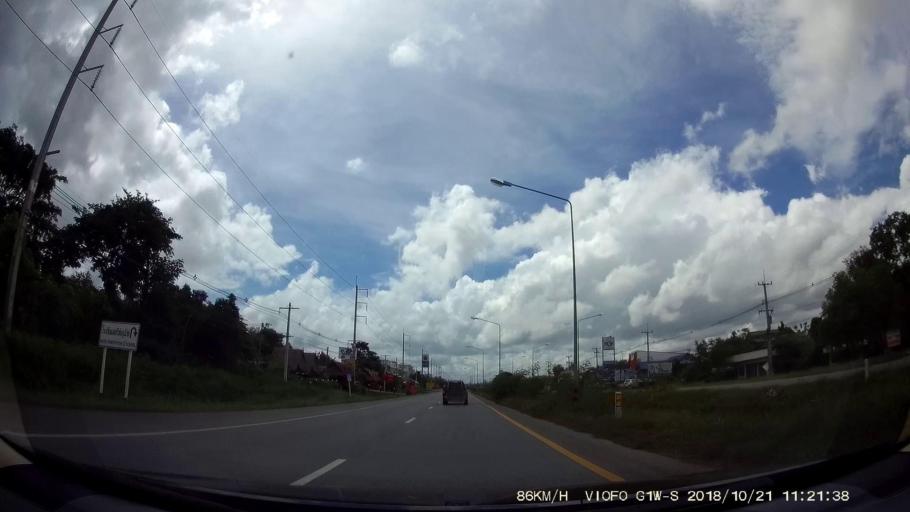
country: TH
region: Chaiyaphum
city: Chaiyaphum
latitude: 15.8443
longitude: 102.0638
